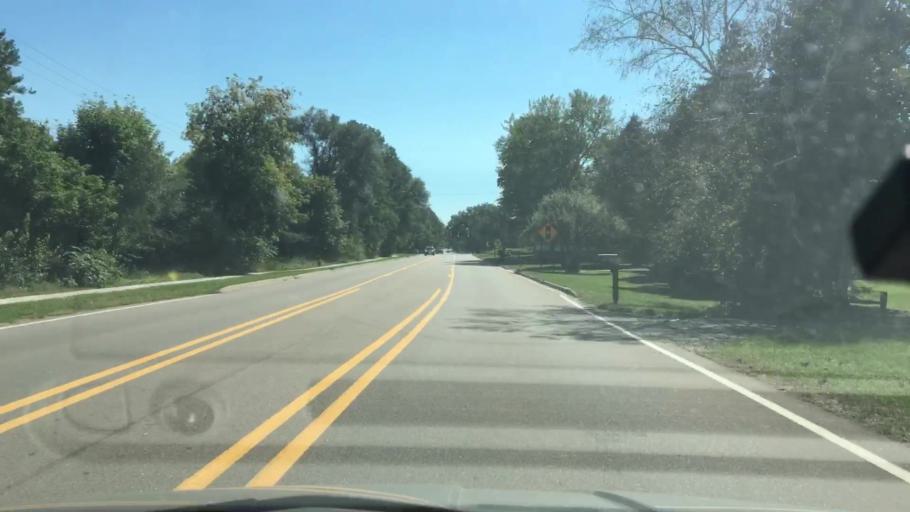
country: US
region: Michigan
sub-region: Livingston County
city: Brighton
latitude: 42.5096
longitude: -83.7690
